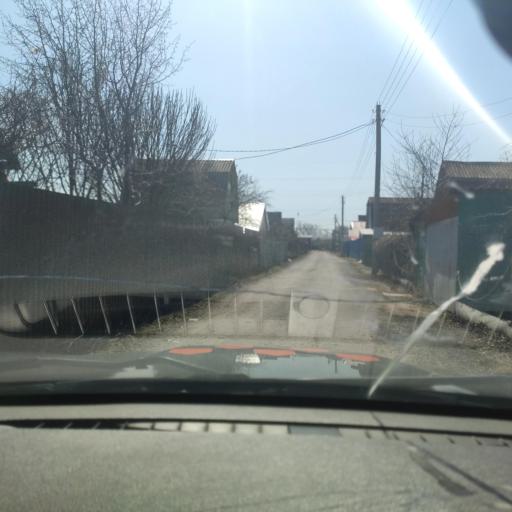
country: RU
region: Samara
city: Podstepki
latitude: 53.5991
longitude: 49.2154
